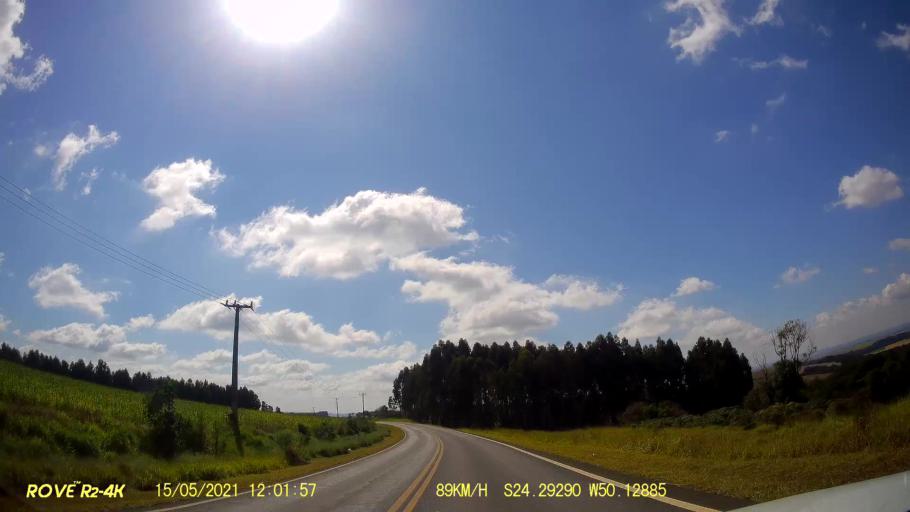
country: BR
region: Parana
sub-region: Pirai Do Sul
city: Pirai do Sul
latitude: -24.2930
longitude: -50.1290
